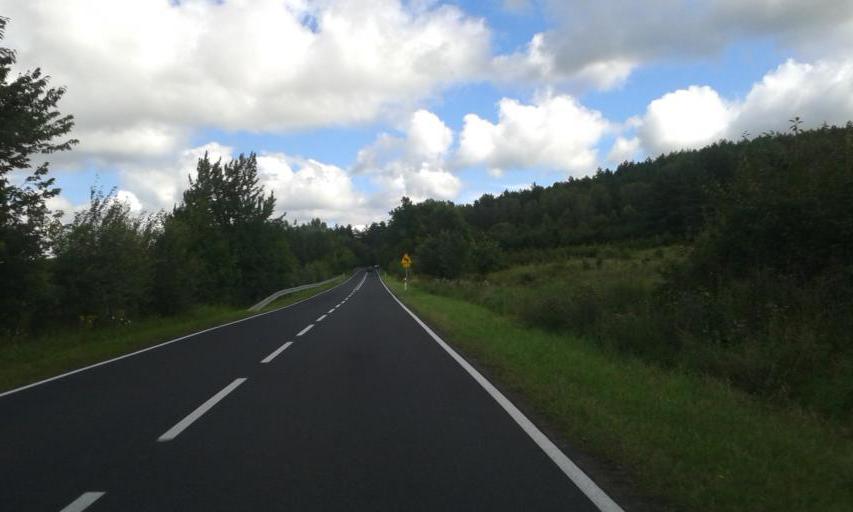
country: PL
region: West Pomeranian Voivodeship
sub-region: Powiat koszalinski
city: Polanow
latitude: 54.0098
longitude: 16.7172
